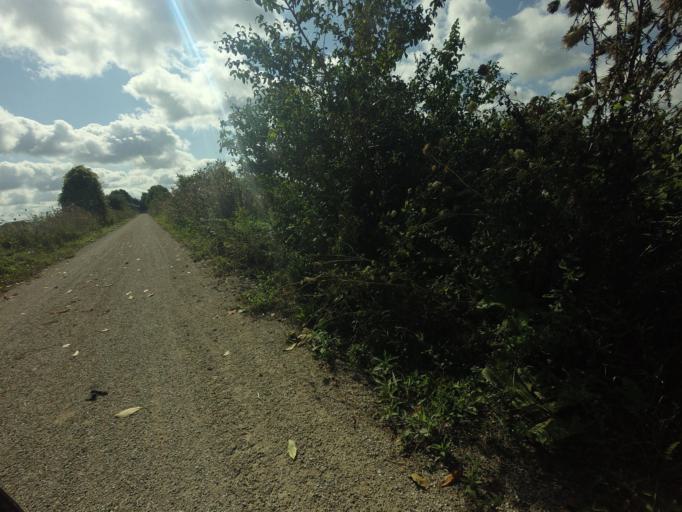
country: CA
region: Ontario
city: Huron East
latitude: 43.7173
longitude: -81.3897
